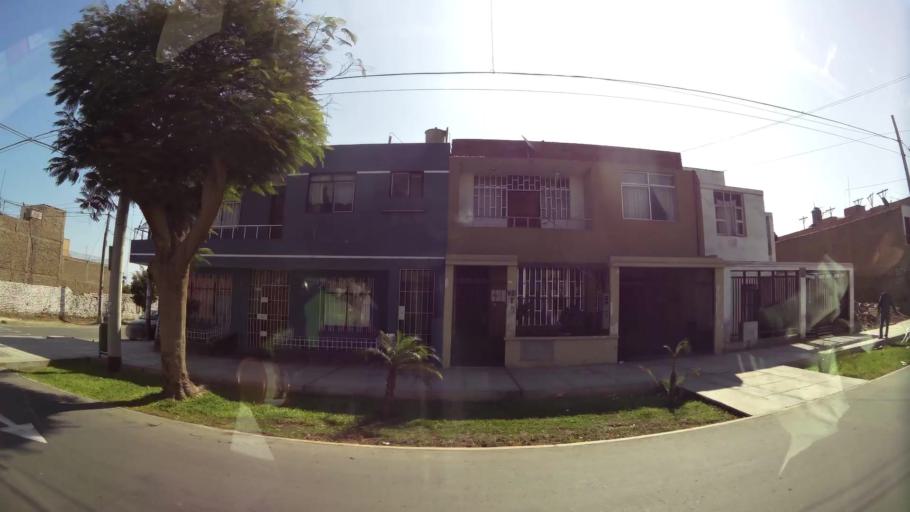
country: PE
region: Ica
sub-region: Provincia de Chincha
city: Chincha Alta
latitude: -13.4115
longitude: -76.1300
